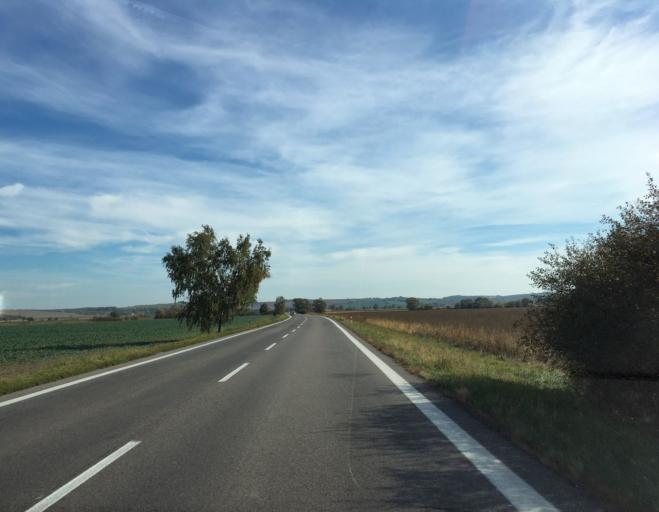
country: SK
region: Nitriansky
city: Zeliezovce
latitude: 48.1252
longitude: 18.6687
